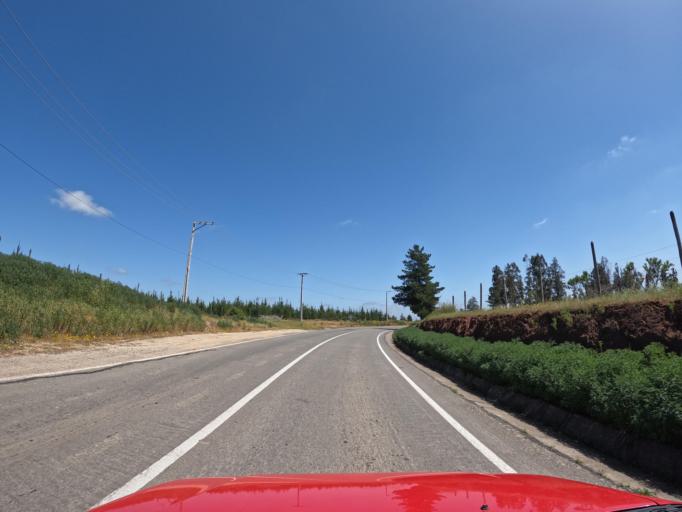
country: CL
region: O'Higgins
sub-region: Provincia de Colchagua
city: Santa Cruz
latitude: -34.6590
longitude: -71.8557
